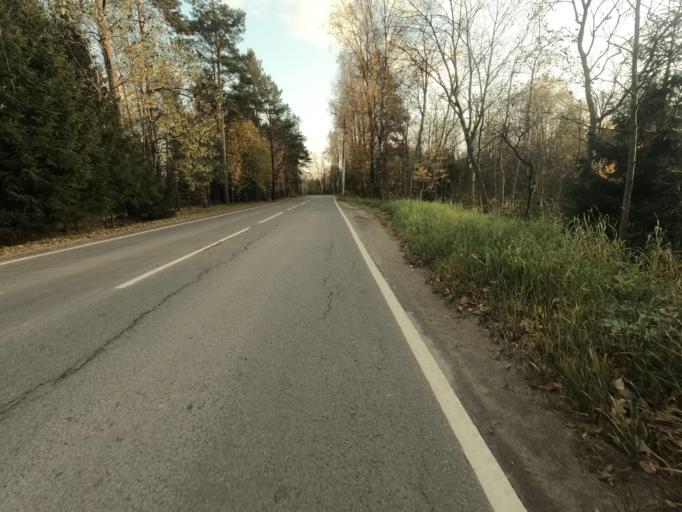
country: RU
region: St.-Petersburg
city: Beloostrov
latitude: 60.1596
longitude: 30.0059
